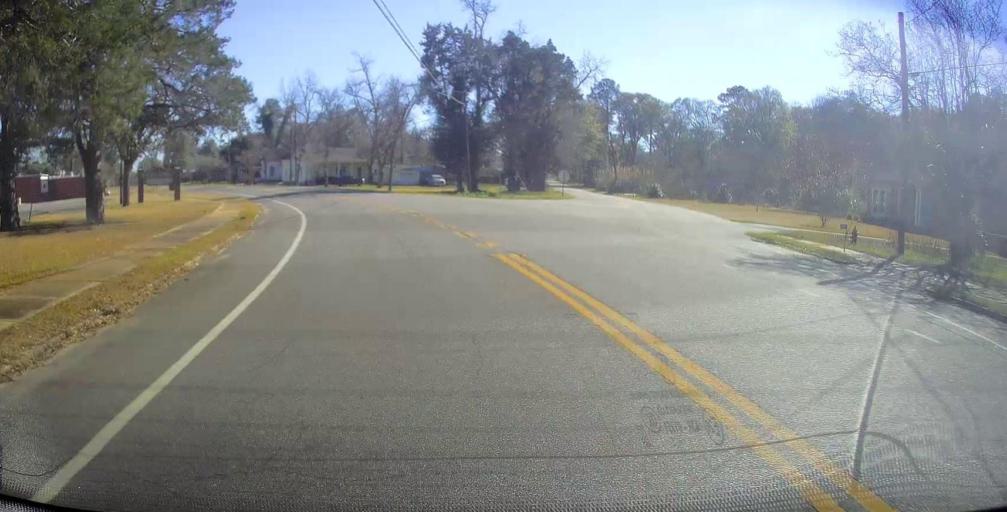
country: US
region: Georgia
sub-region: Macon County
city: Oglethorpe
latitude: 32.2994
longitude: -84.0658
